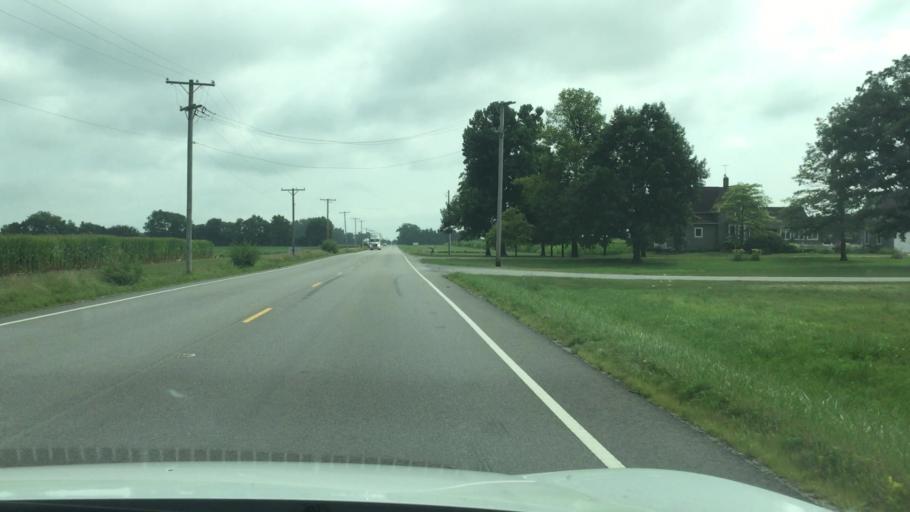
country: US
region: Ohio
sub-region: Union County
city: Marysville
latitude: 40.1657
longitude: -83.4465
